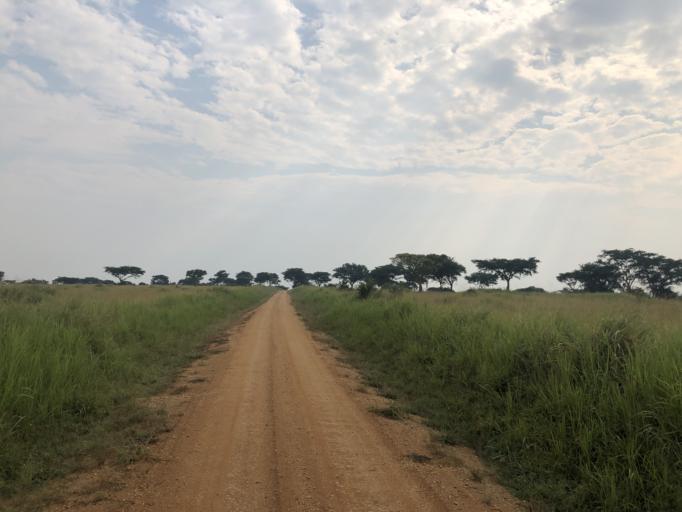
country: UG
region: Western Region
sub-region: Mitoma District
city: Mitoma
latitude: -0.5127
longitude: 29.8020
